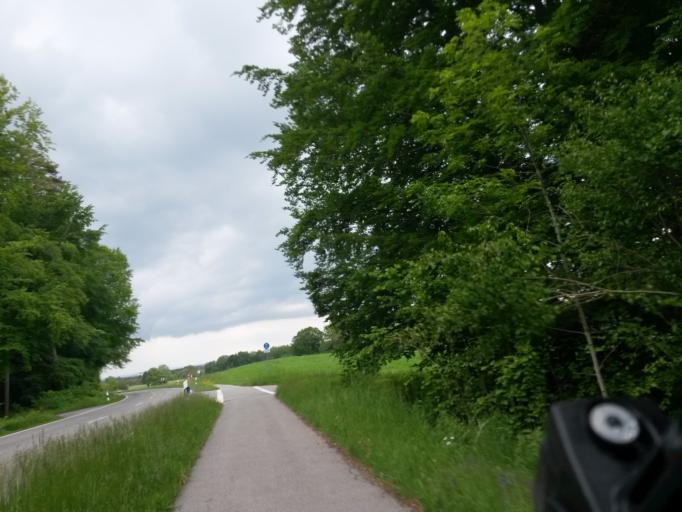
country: DE
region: Baden-Wuerttemberg
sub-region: Tuebingen Region
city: Bad Waldsee
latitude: 47.9233
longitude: 9.7762
